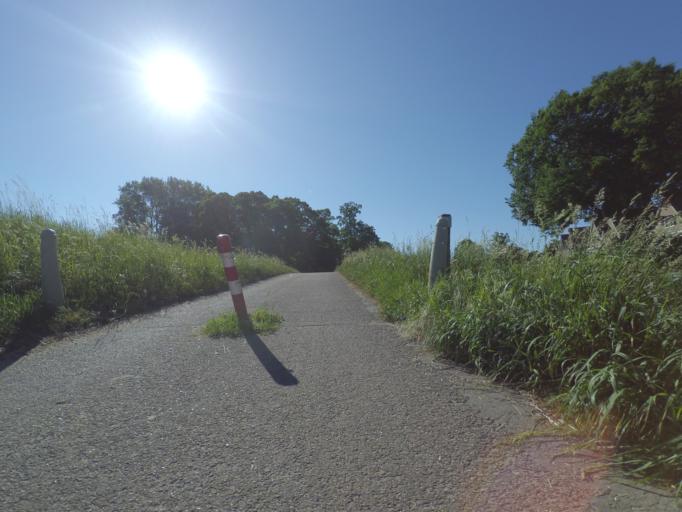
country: NL
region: Overijssel
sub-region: Gemeente Deventer
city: Deventer
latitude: 52.2523
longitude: 6.1437
